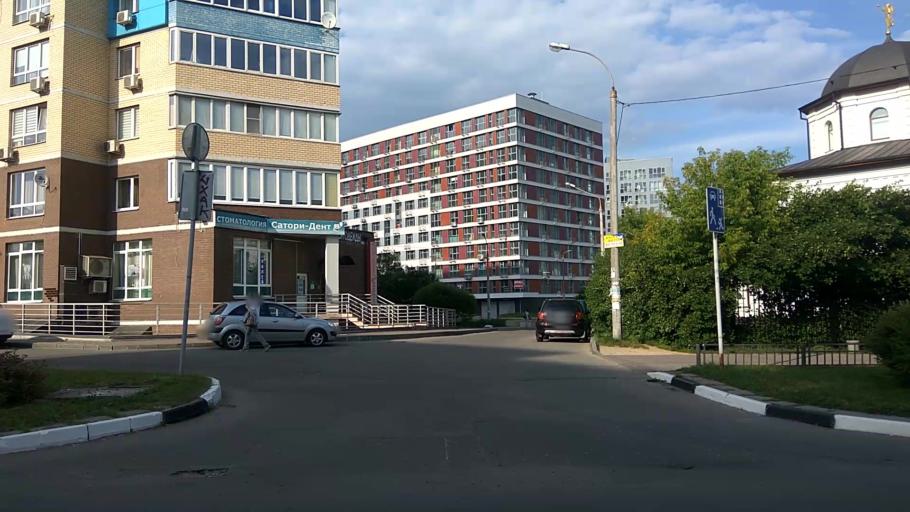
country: RU
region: Moskovskaya
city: Mytishchi
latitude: 55.9171
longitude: 37.7466
